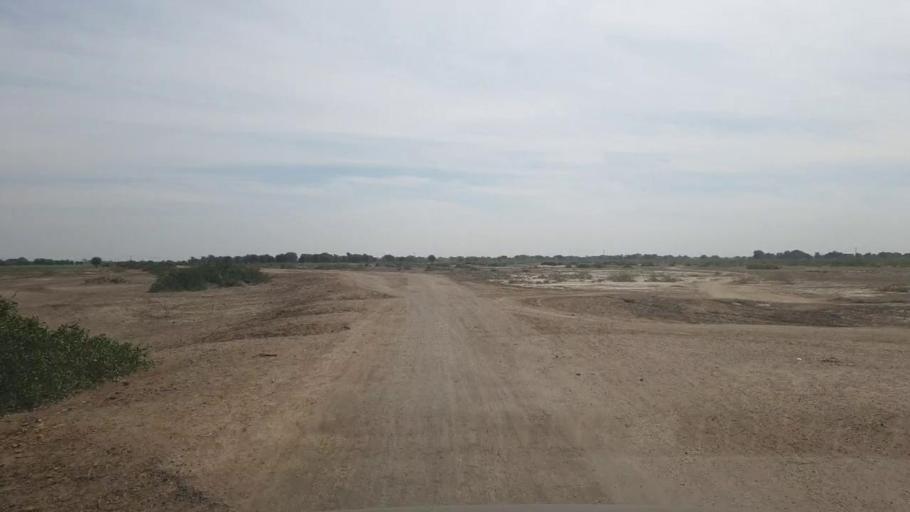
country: PK
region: Sindh
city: Kunri
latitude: 25.2990
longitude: 69.5772
